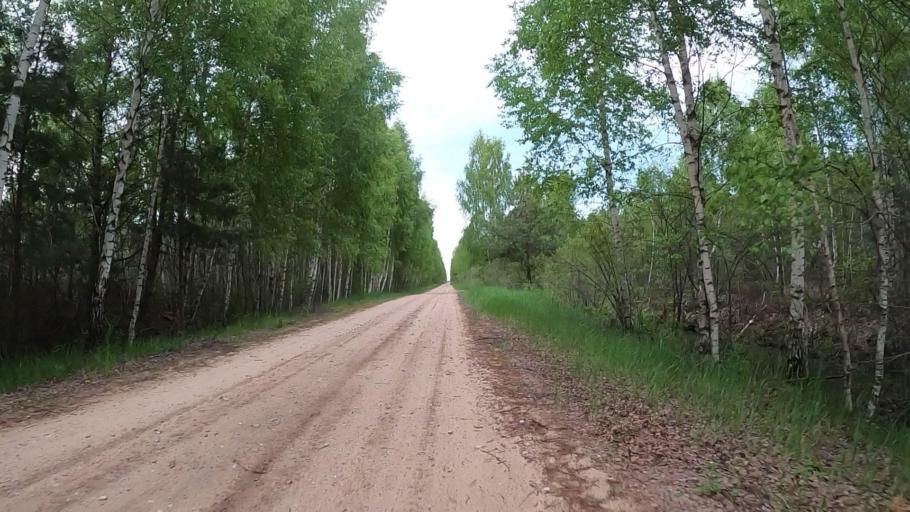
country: LV
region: Olaine
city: Olaine
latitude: 56.8478
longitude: 23.9396
